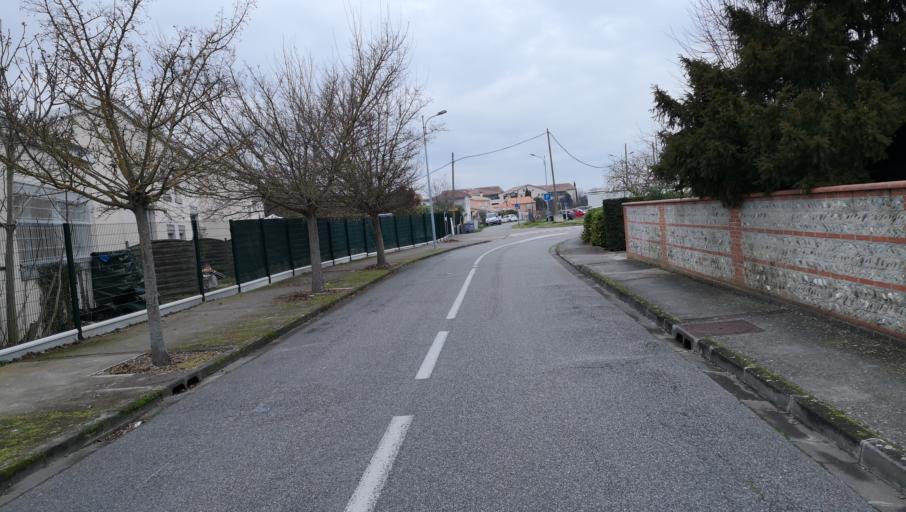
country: FR
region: Midi-Pyrenees
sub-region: Departement de la Haute-Garonne
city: Blagnac
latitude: 43.6453
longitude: 1.3809
